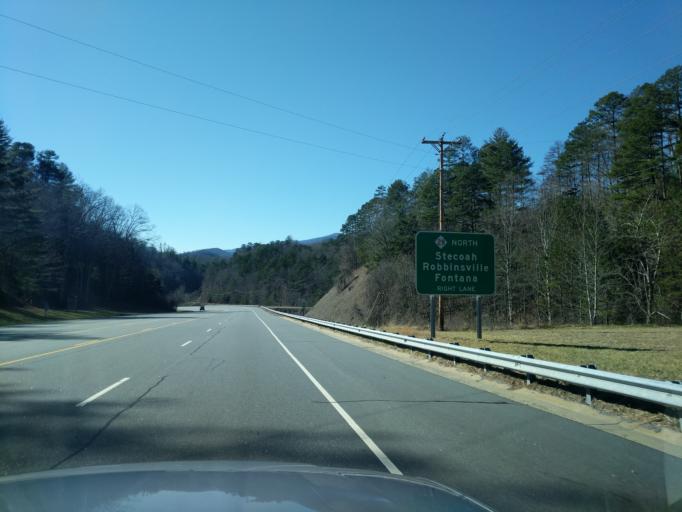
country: US
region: North Carolina
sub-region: Swain County
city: Bryson City
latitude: 35.3683
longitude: -83.5449
